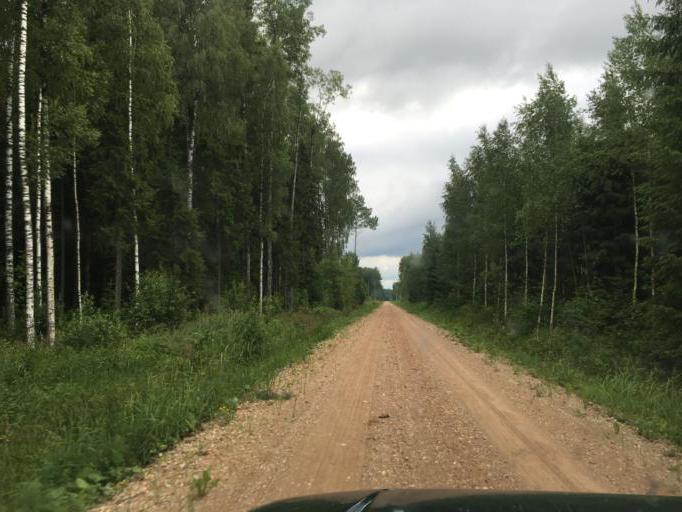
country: LV
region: Vilaka
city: Vilaka
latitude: 57.3871
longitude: 27.4985
